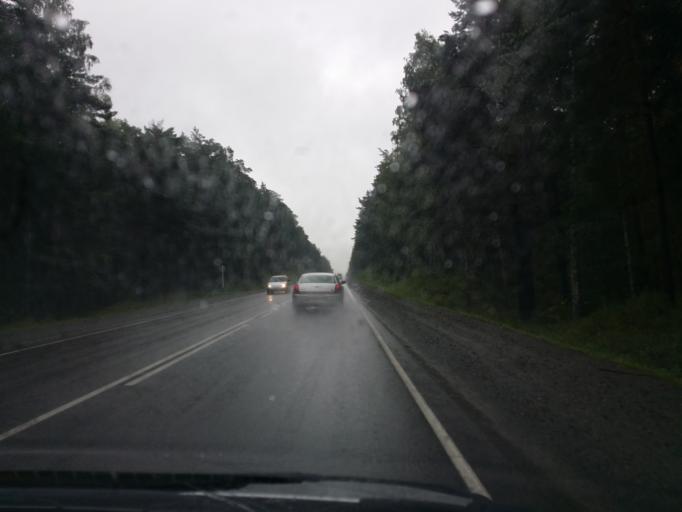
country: RU
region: Altai Krai
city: Bayunovskiye Klyuchi
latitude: 53.3214
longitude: 84.1954
